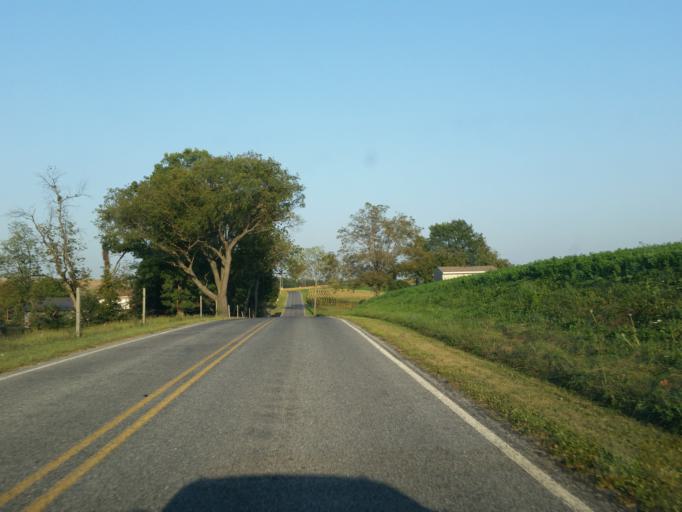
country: US
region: Pennsylvania
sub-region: Lebanon County
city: Cleona
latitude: 40.3632
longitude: -76.4996
